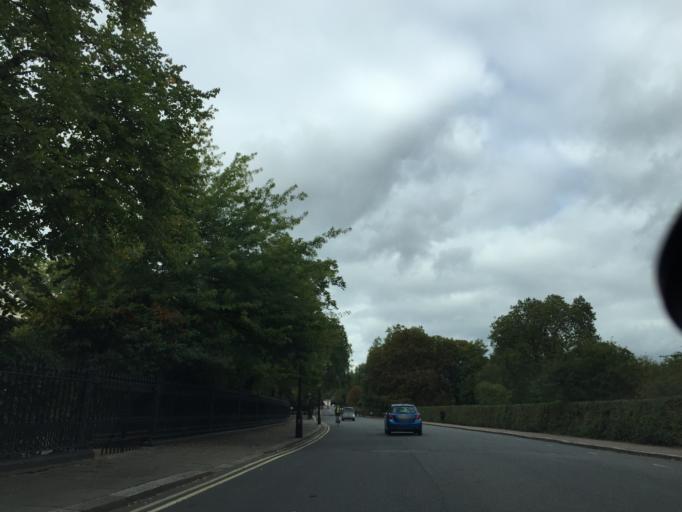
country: GB
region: England
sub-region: Greater London
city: Camden Town
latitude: 51.5264
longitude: -0.1600
